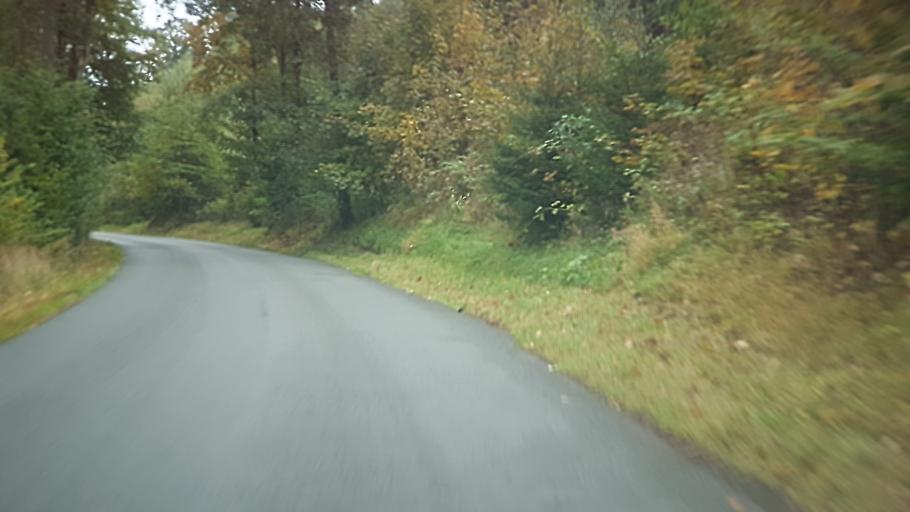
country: DE
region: North Rhine-Westphalia
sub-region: Regierungsbezirk Arnsberg
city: Luedenscheid
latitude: 51.2158
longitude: 7.6773
